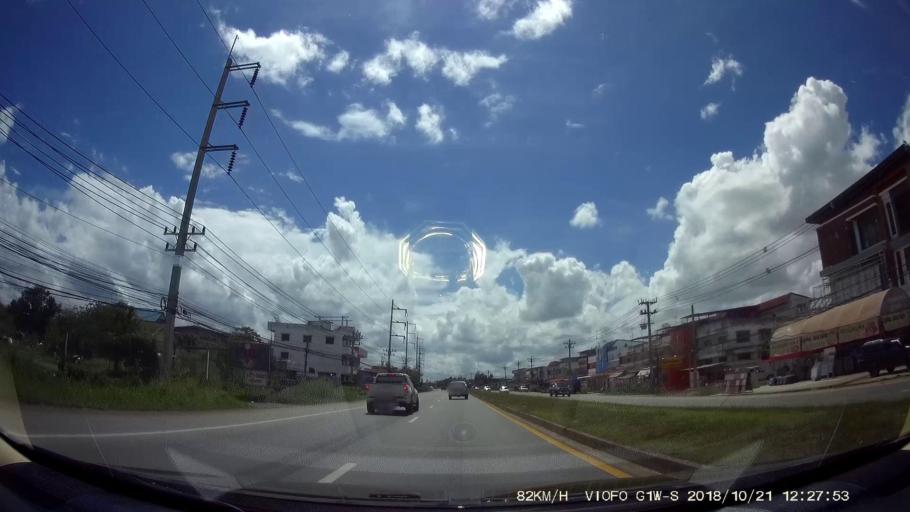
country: TH
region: Nakhon Ratchasima
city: Dan Khun Thot
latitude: 15.1962
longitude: 101.7625
